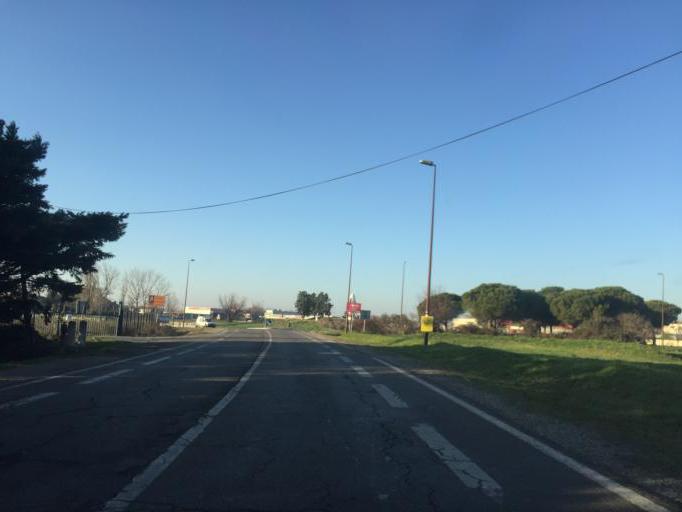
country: FR
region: Provence-Alpes-Cote d'Azur
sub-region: Departement du Vaucluse
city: Le Pontet
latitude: 43.9488
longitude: 4.8606
